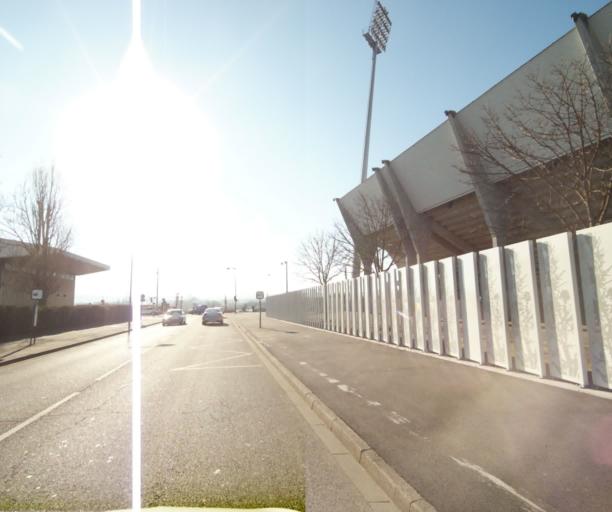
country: FR
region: Lorraine
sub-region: Departement de Meurthe-et-Moselle
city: Saint-Max
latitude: 48.6946
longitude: 6.2114
